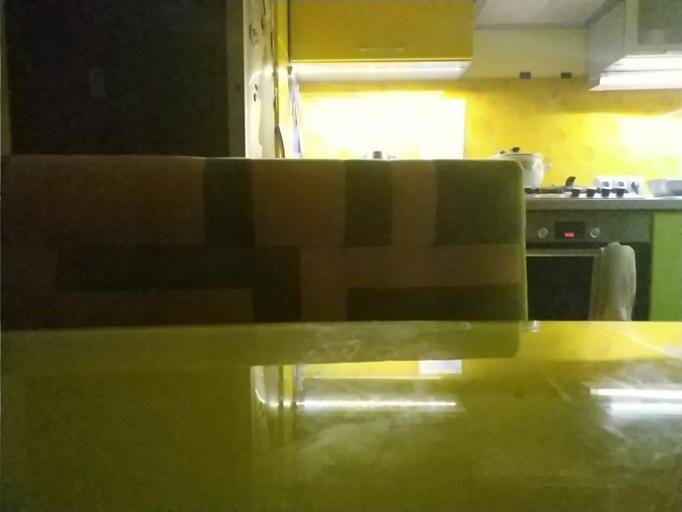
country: RU
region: Republic of Karelia
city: Pyaozerskiy
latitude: 65.6158
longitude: 30.5572
